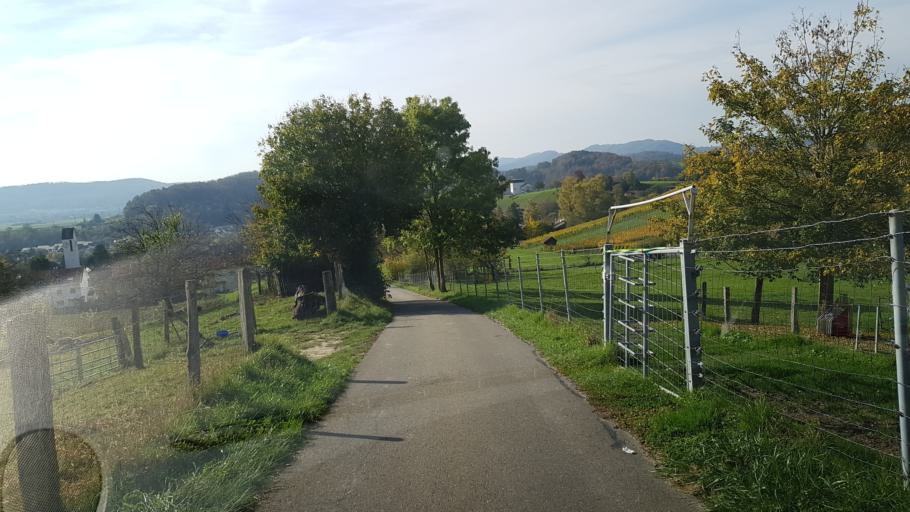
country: CH
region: Aargau
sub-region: Bezirk Baden
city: Birmenstorf
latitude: 47.4646
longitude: 8.2530
